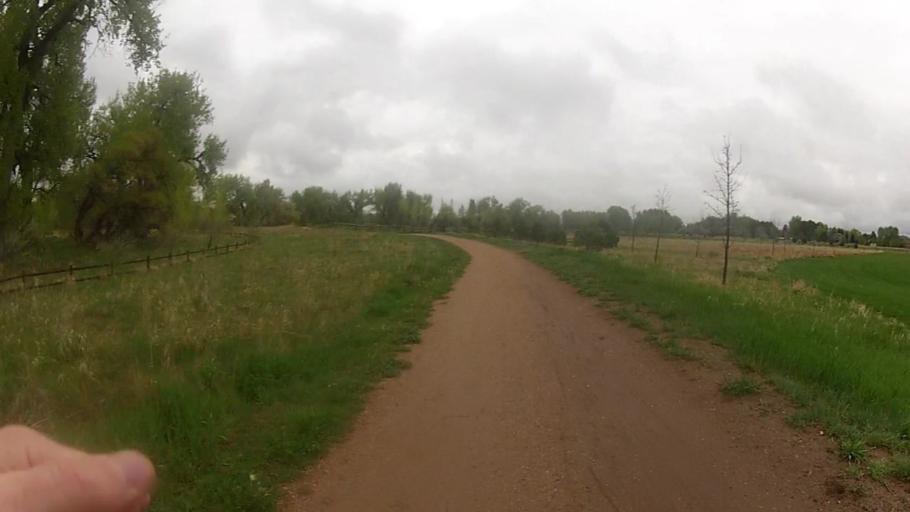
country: US
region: Colorado
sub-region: Larimer County
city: Fort Collins
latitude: 40.5440
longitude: -105.1275
